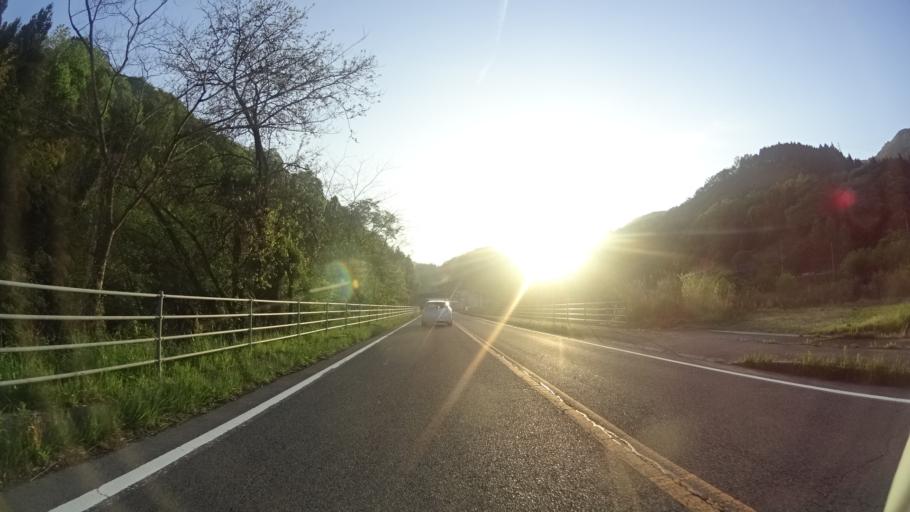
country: JP
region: Tokushima
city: Ikedacho
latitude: 34.0047
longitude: 133.7140
